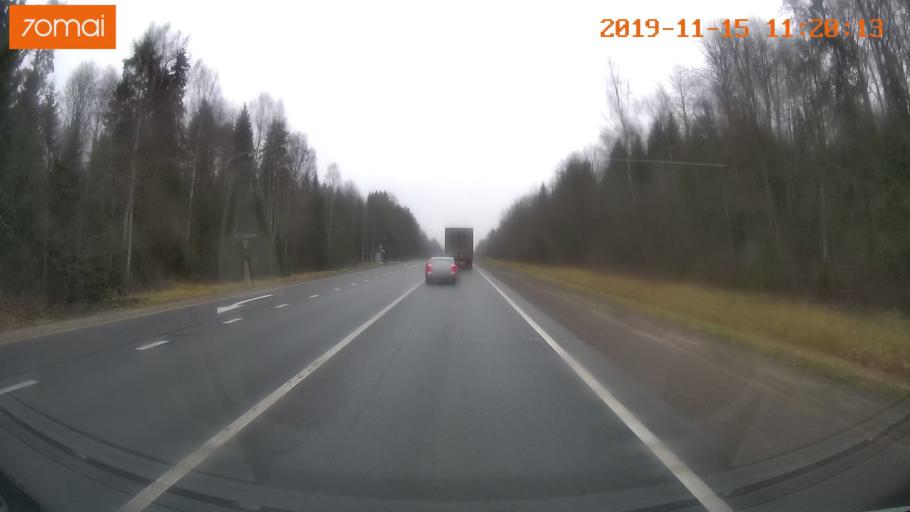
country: RU
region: Vologda
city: Molochnoye
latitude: 59.1410
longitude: 39.3107
